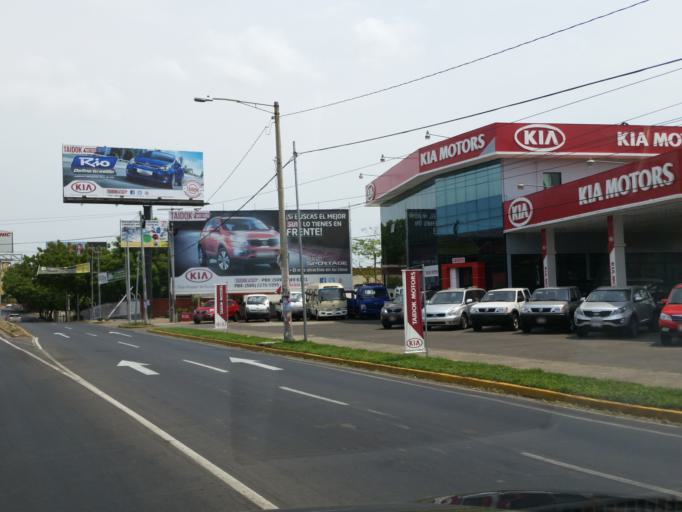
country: NI
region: Managua
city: Managua
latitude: 12.1114
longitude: -86.2534
